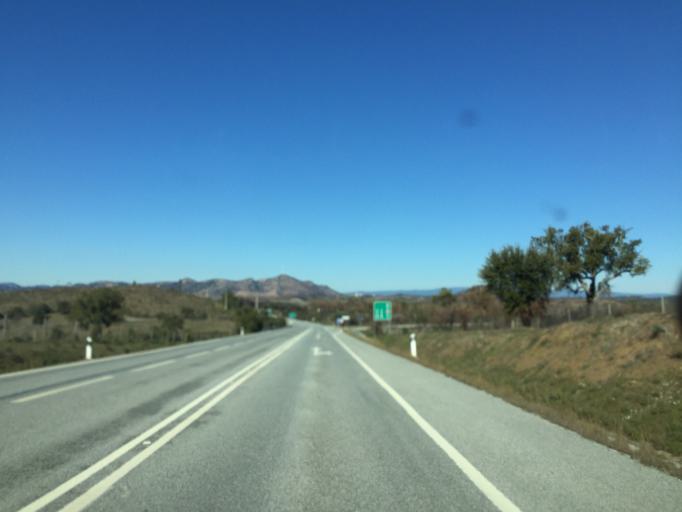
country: PT
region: Portalegre
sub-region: Nisa
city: Nisa
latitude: 39.5290
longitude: -7.7872
